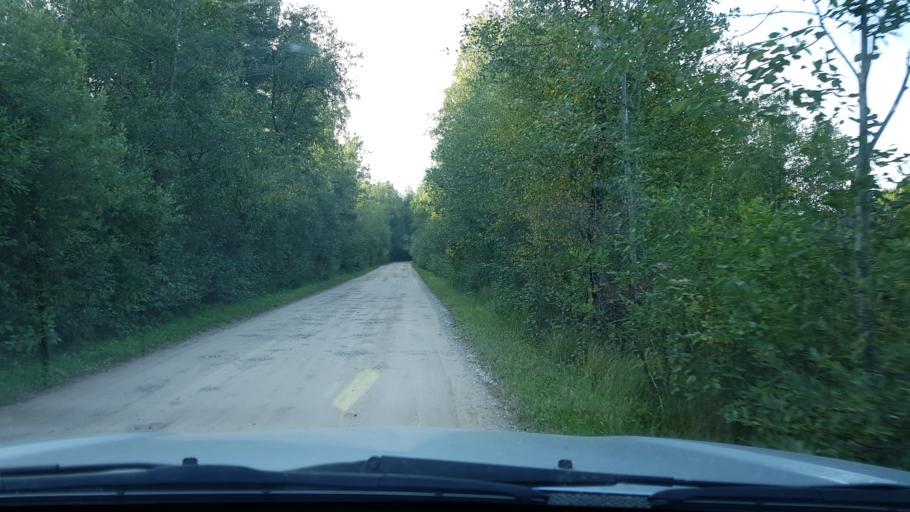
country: EE
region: Ida-Virumaa
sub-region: Sillamaee linn
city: Sillamae
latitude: 59.2601
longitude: 27.9236
